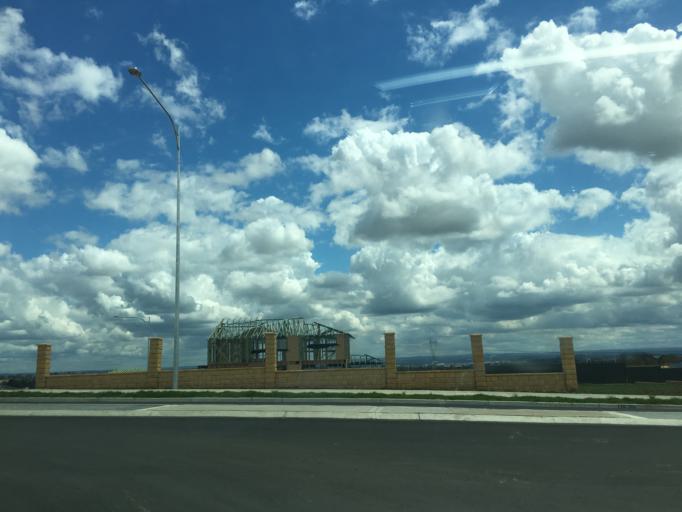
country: AU
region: New South Wales
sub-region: Campbelltown Municipality
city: Denham Court
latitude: -33.9885
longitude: 150.7985
